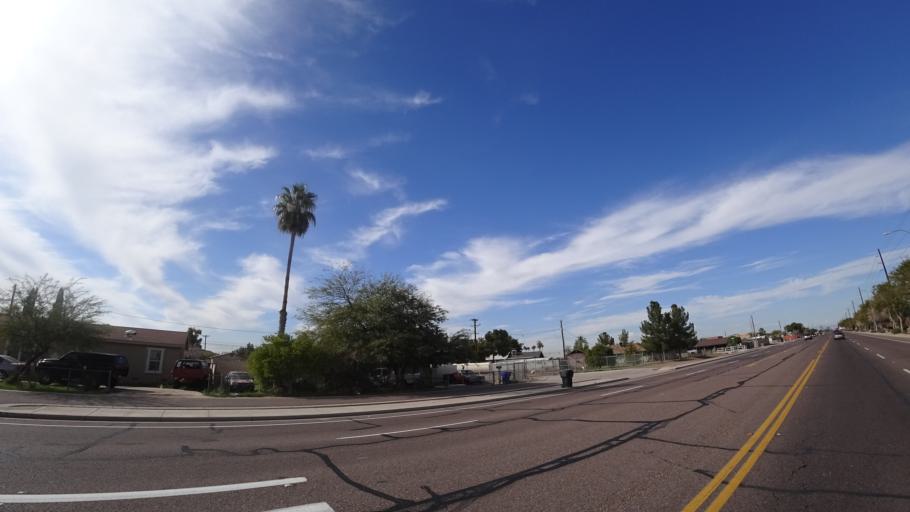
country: US
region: Arizona
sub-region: Maricopa County
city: Tolleson
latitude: 33.4286
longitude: -112.2897
